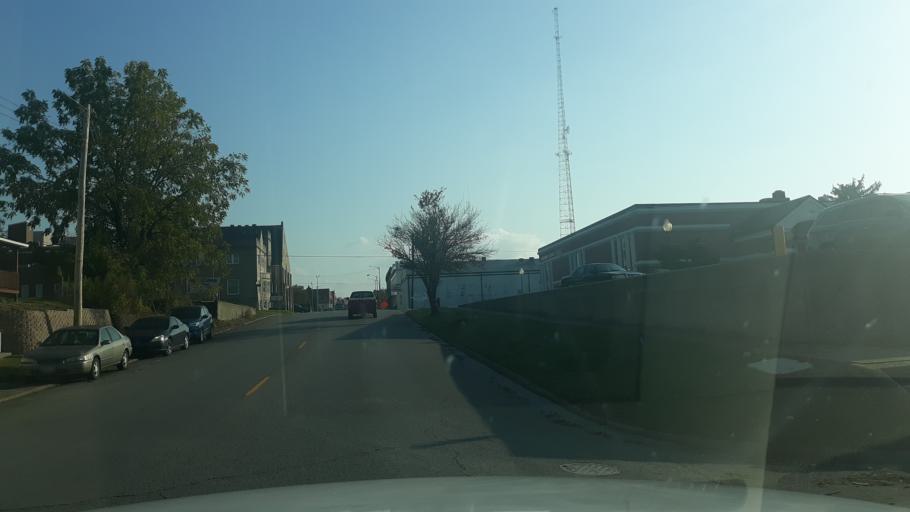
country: US
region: Illinois
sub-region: Saline County
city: Harrisburg
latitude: 37.7412
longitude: -88.5403
